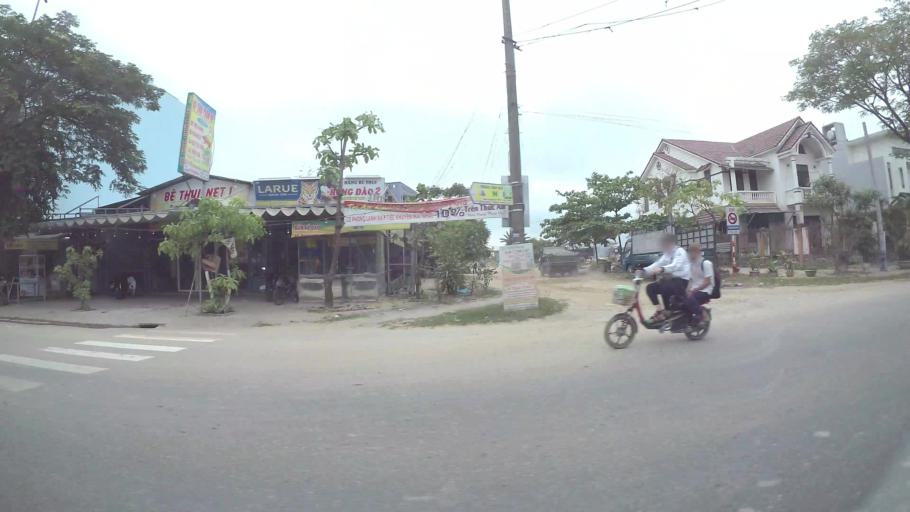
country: VN
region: Da Nang
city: Lien Chieu
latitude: 16.0732
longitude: 108.1744
